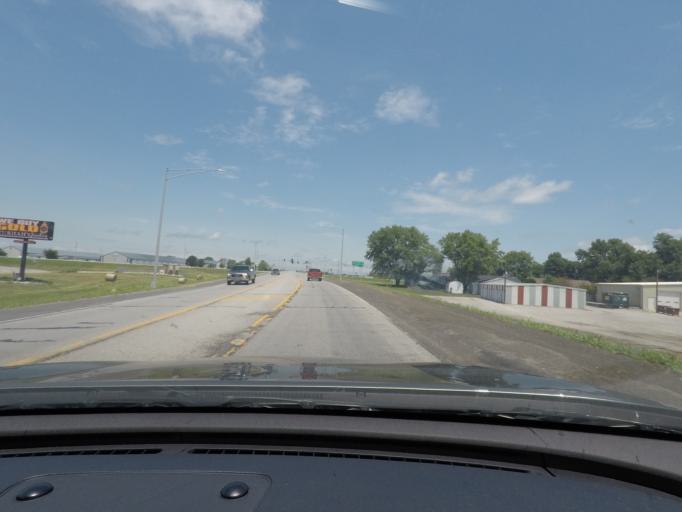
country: US
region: Missouri
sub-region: Saline County
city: Marshall
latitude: 39.1181
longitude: -93.2130
